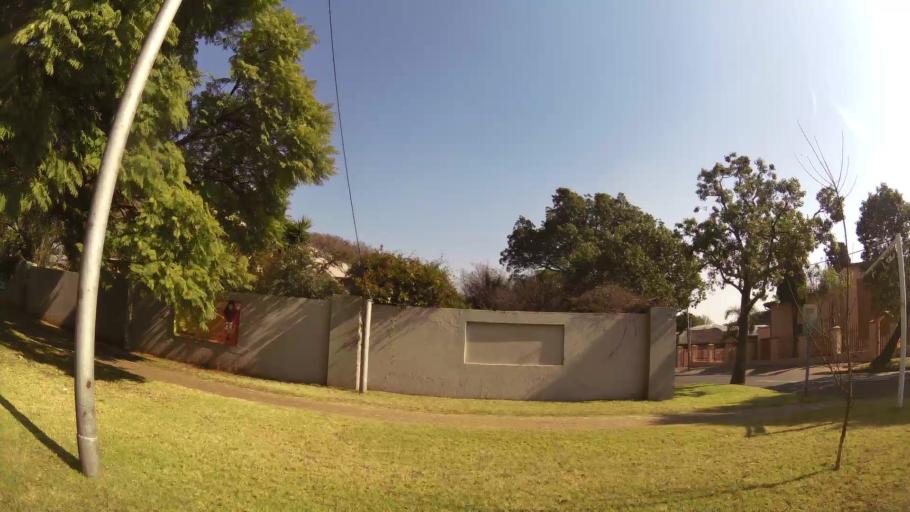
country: ZA
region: Gauteng
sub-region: Ekurhuleni Metropolitan Municipality
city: Benoni
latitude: -26.1981
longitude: 28.3004
